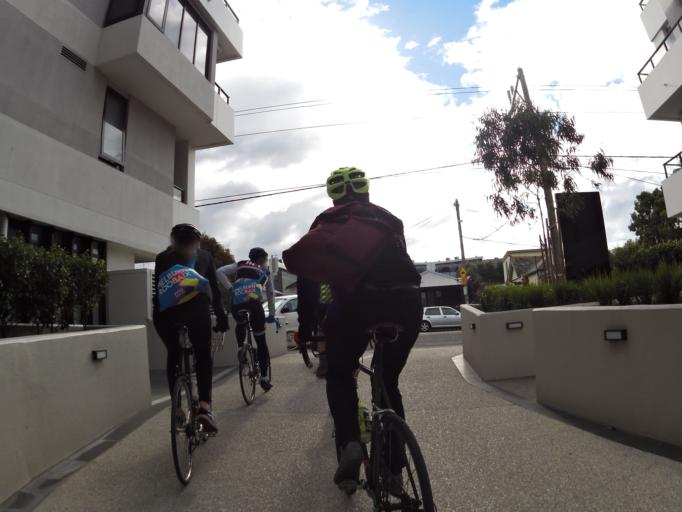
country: AU
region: Victoria
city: Brunswick East
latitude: -37.7782
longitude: 144.9763
